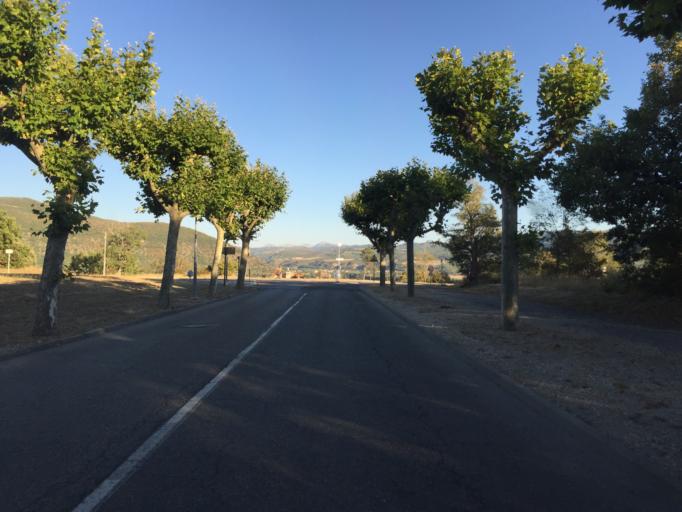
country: FR
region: Provence-Alpes-Cote d'Azur
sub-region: Departement des Alpes-de-Haute-Provence
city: Malijai
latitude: 44.0687
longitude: 5.9964
